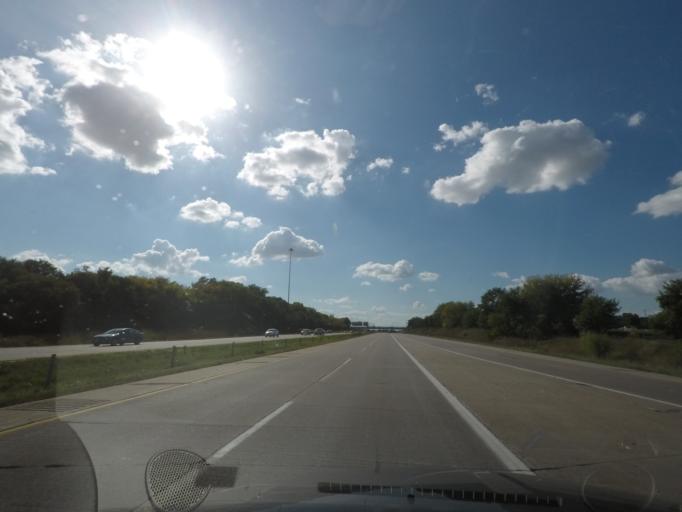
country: US
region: Iowa
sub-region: Polk County
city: Clive
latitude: 41.5923
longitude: -93.7843
